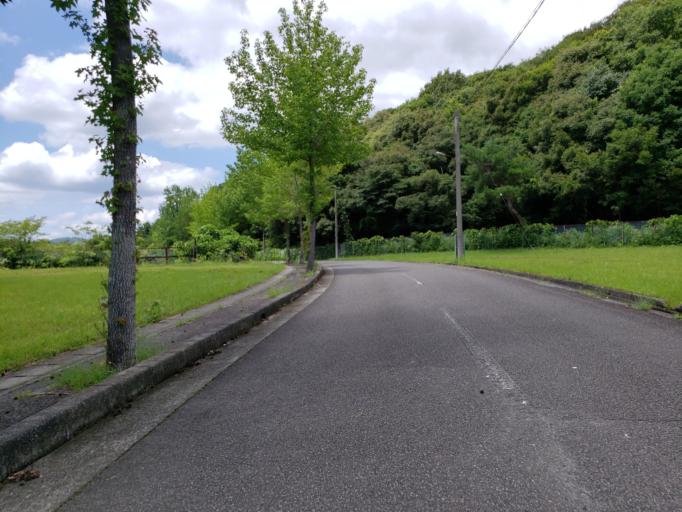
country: JP
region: Hyogo
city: Himeji
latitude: 34.8631
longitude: 134.7529
